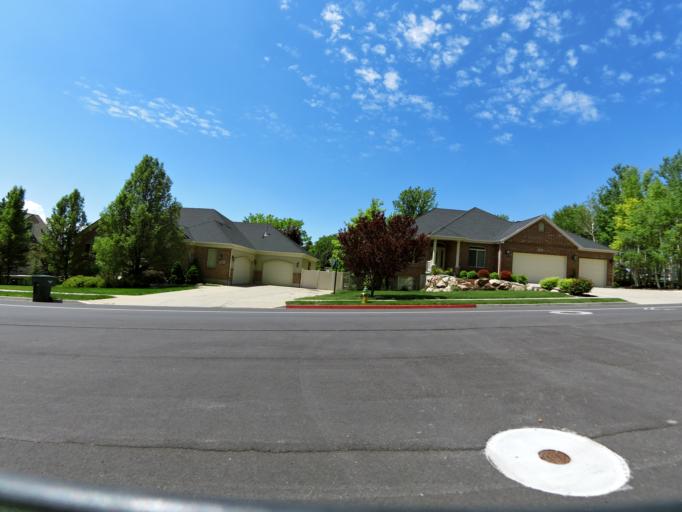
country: US
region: Utah
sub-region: Weber County
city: Uintah
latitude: 41.1649
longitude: -111.9254
